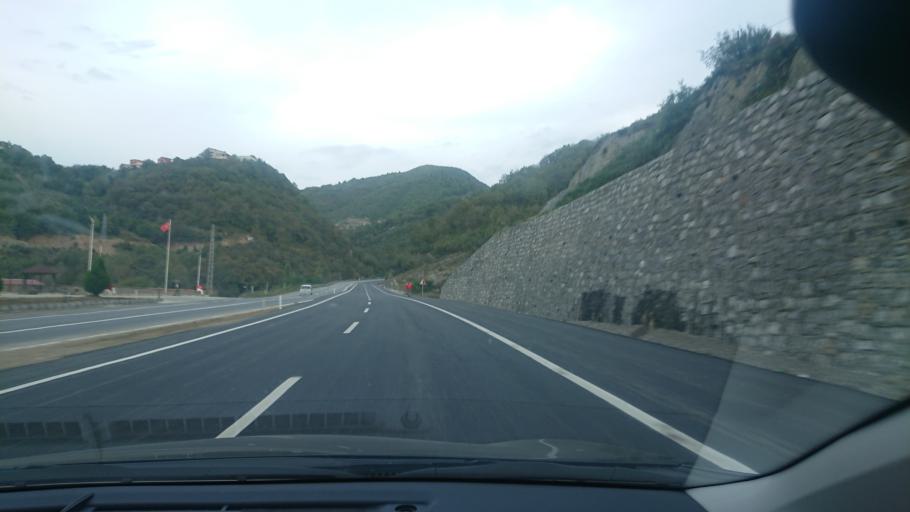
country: TR
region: Zonguldak
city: Beycuma
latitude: 41.3854
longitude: 31.9408
